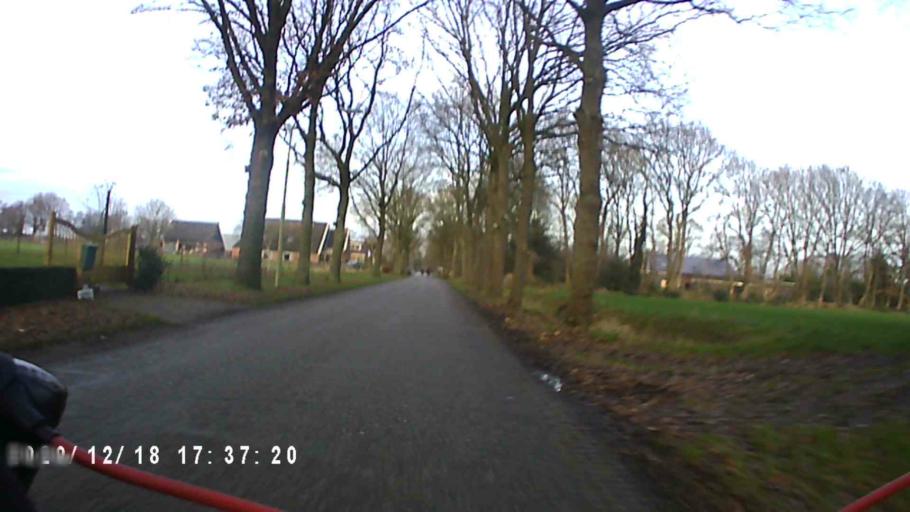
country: NL
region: Drenthe
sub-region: Gemeente Tynaarlo
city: Vries
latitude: 53.0844
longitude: 6.5753
